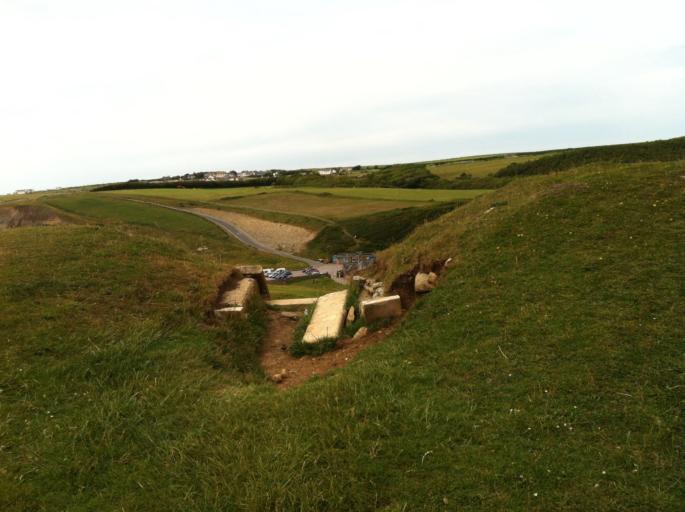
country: GB
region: Wales
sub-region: Bridgend county borough
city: Merthyr Mawr
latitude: 51.4441
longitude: -3.6041
